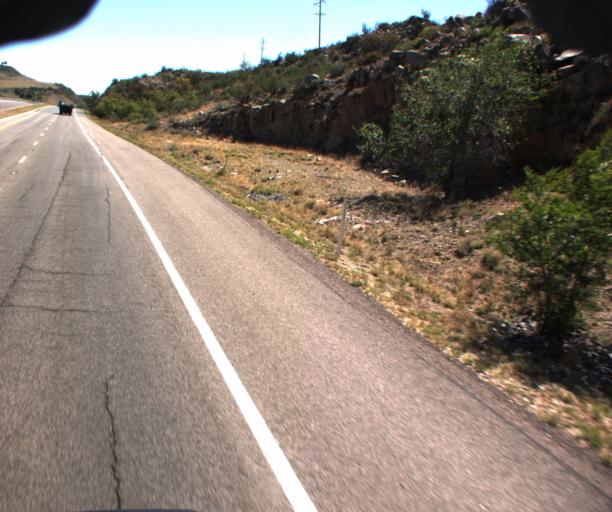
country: US
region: Arizona
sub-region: Yavapai County
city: Prescott
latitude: 34.5641
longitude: -112.4443
